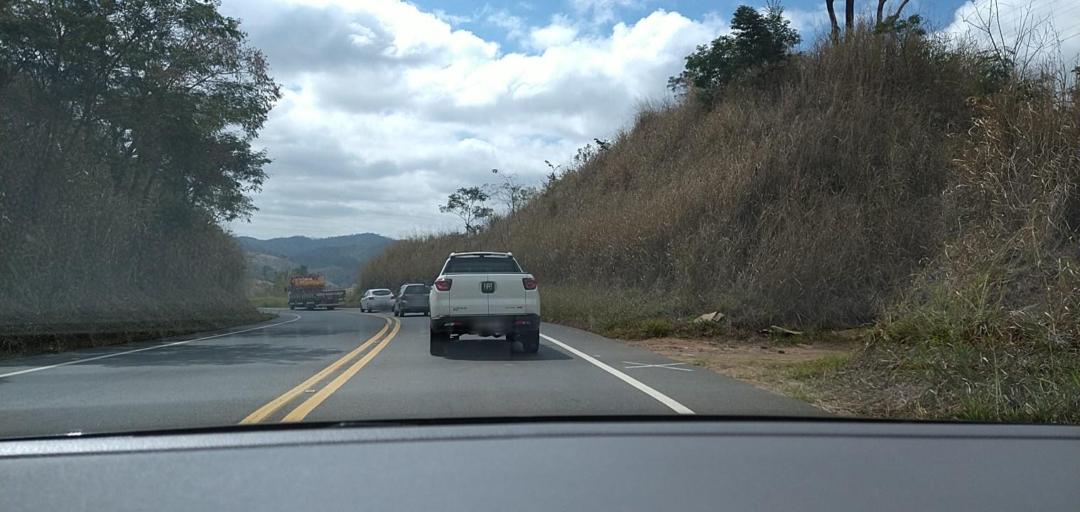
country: BR
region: Minas Gerais
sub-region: Ponte Nova
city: Ponte Nova
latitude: -20.5118
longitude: -42.8856
